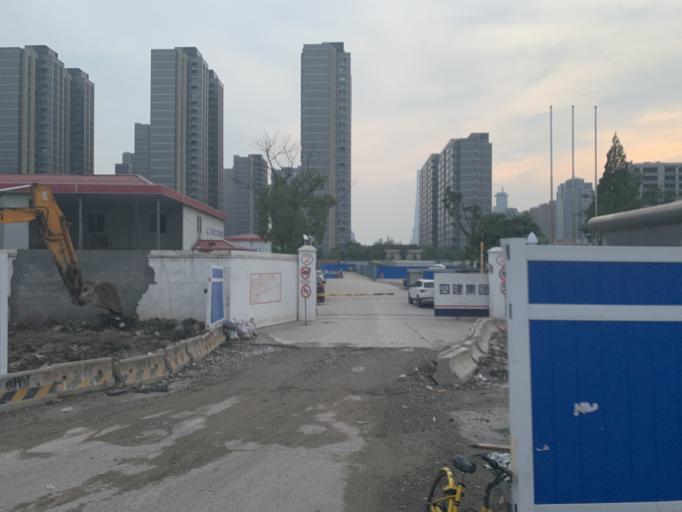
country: CN
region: Shanghai Shi
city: Pudong
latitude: 31.2436
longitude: 121.5371
